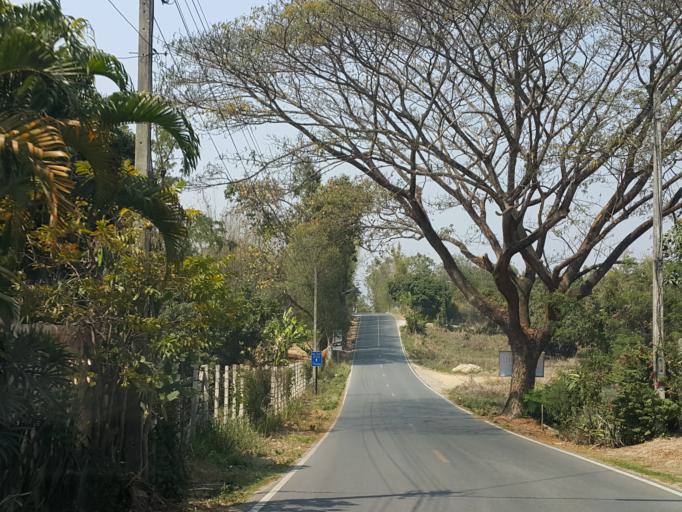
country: TH
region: Chiang Mai
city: San Sai
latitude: 18.9359
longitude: 98.9370
